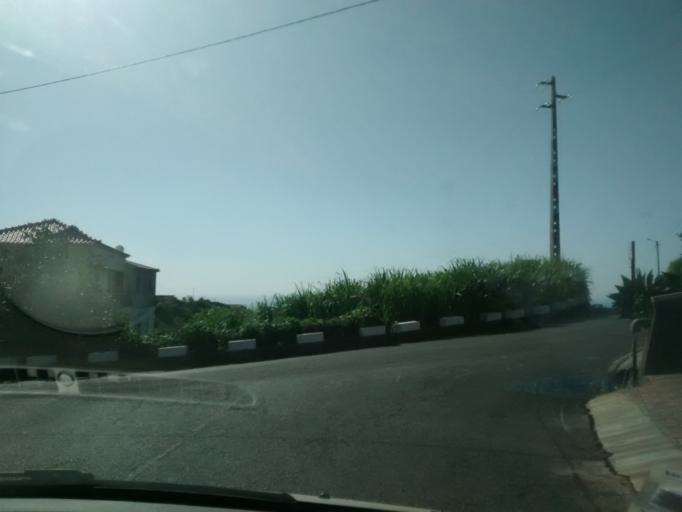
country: PT
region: Madeira
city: Calheta
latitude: 32.7242
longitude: -17.1670
